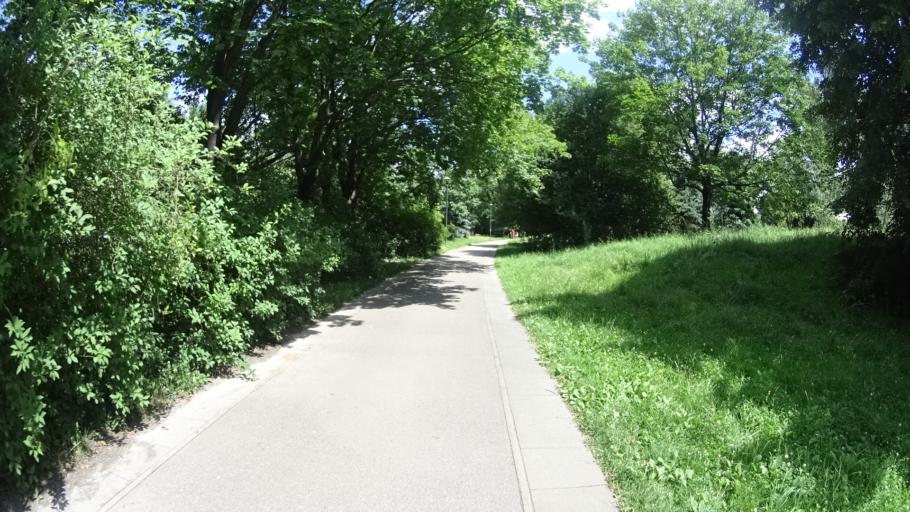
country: PL
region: Masovian Voivodeship
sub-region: Warszawa
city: Ochota
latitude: 52.2113
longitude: 20.9917
